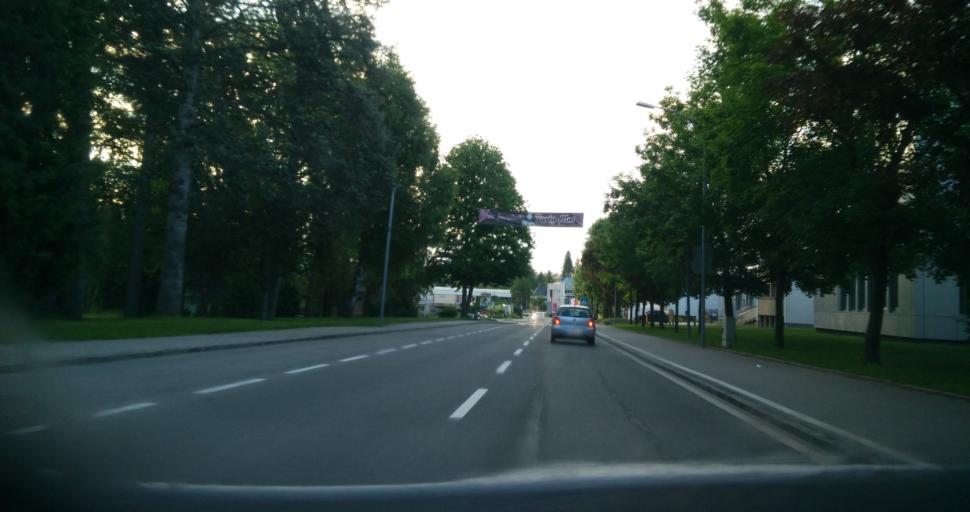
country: AT
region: Carinthia
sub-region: Villach Stadt
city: Villach
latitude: 46.6137
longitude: 13.8326
